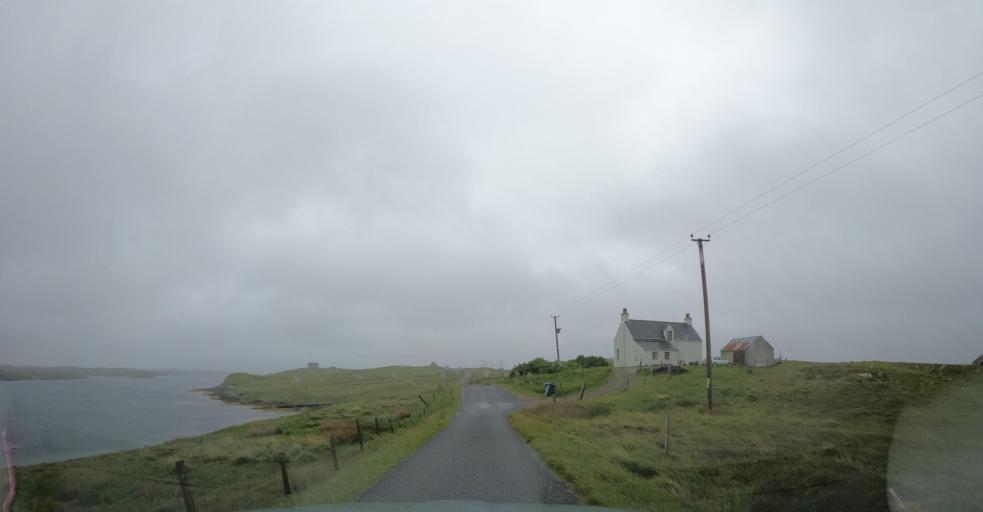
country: GB
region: Scotland
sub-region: Eilean Siar
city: Isle of North Uist
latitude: 57.5503
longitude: -7.2384
